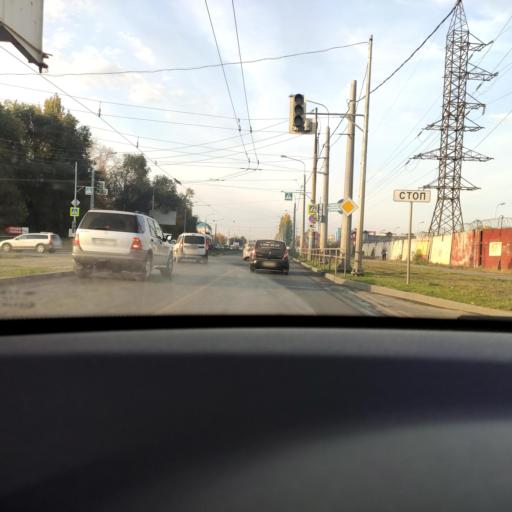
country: RU
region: Samara
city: Samara
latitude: 53.2025
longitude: 50.2647
